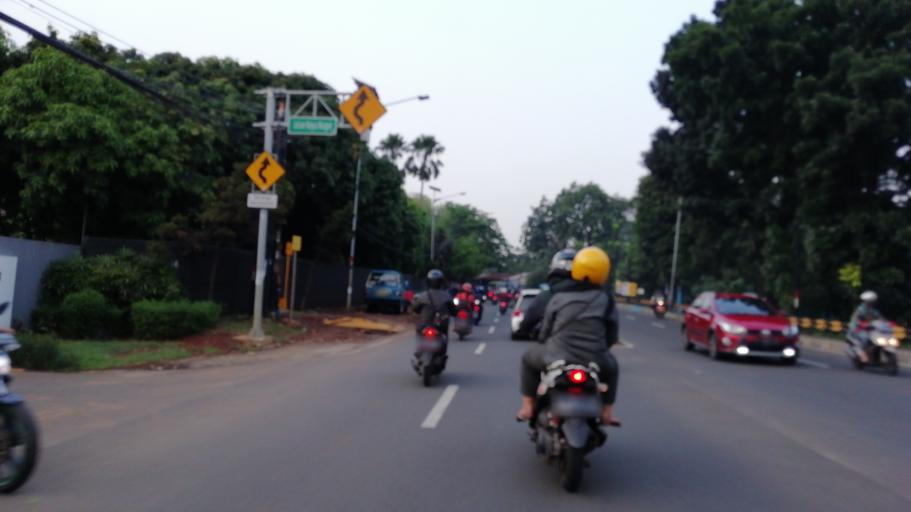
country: ID
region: West Java
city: Depok
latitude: -6.4071
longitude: 106.8621
